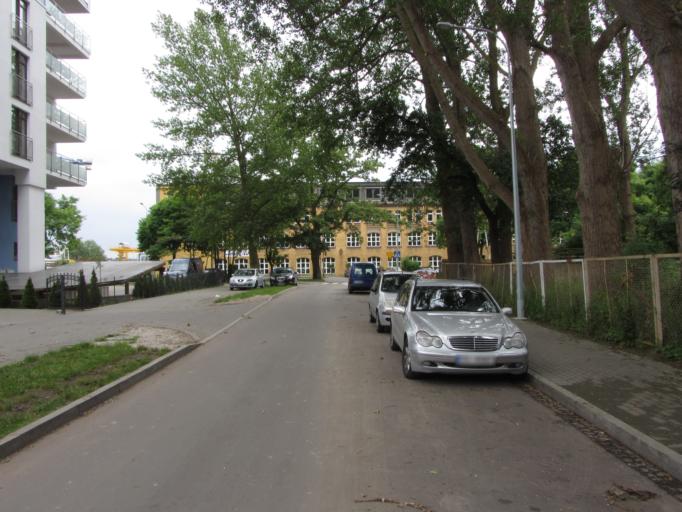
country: PL
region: West Pomeranian Voivodeship
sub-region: Powiat kolobrzeski
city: Kolobrzeg
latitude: 54.1835
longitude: 15.5827
